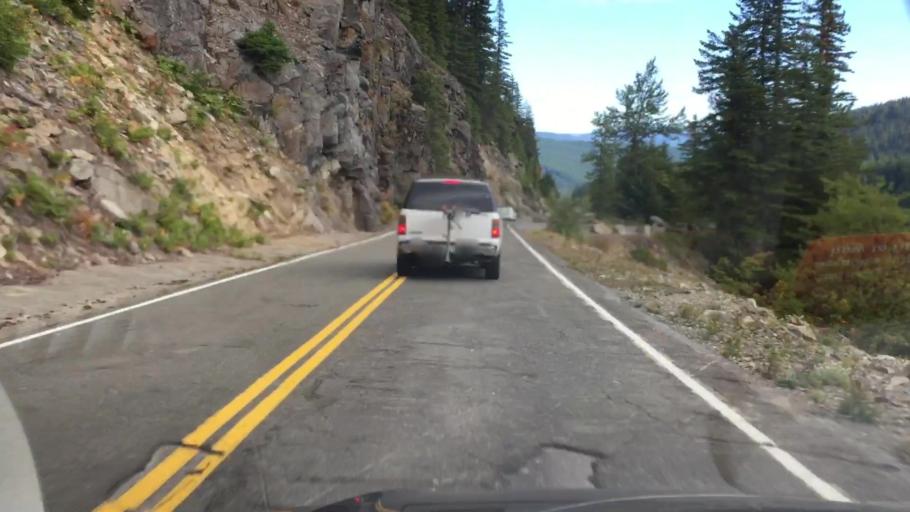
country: US
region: Washington
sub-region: Pierce County
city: Buckley
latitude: 46.7680
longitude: -121.6750
